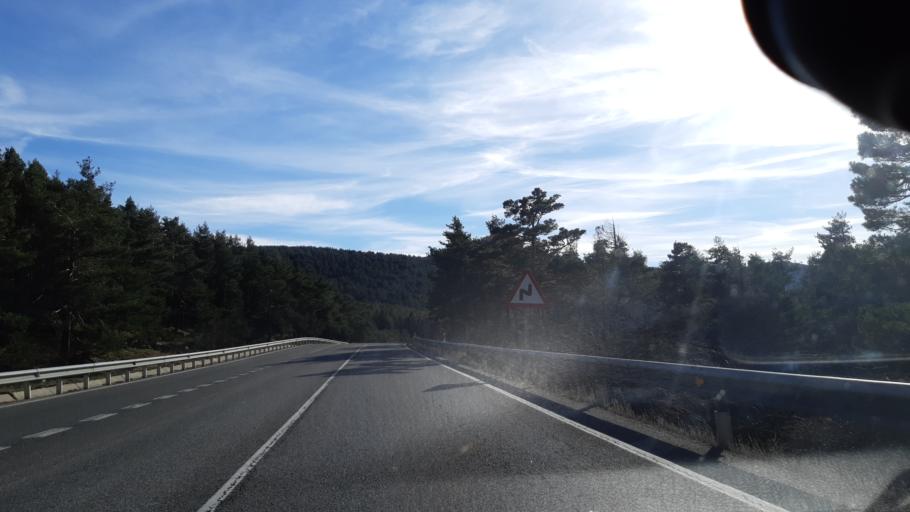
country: ES
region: Madrid
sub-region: Provincia de Madrid
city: Guadarrama
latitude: 40.7084
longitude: -4.1421
